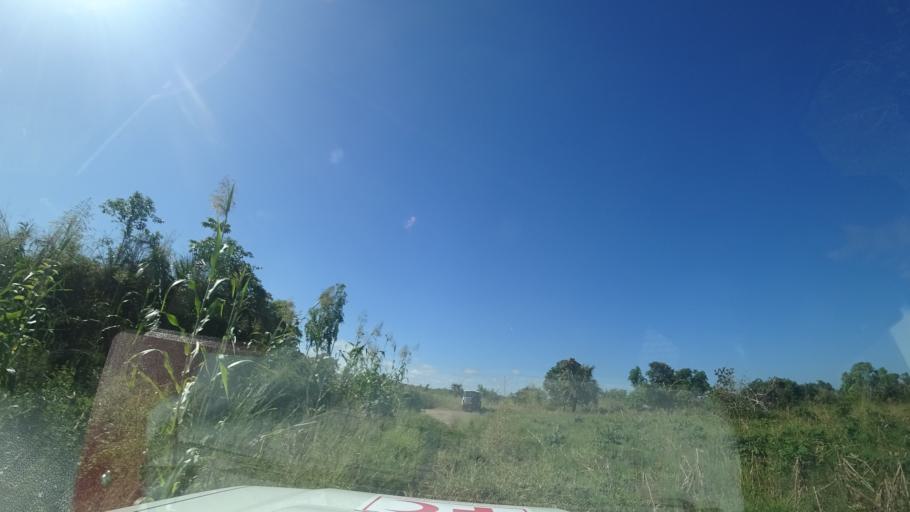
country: MZ
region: Sofala
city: Dondo
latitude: -19.3935
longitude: 34.5929
